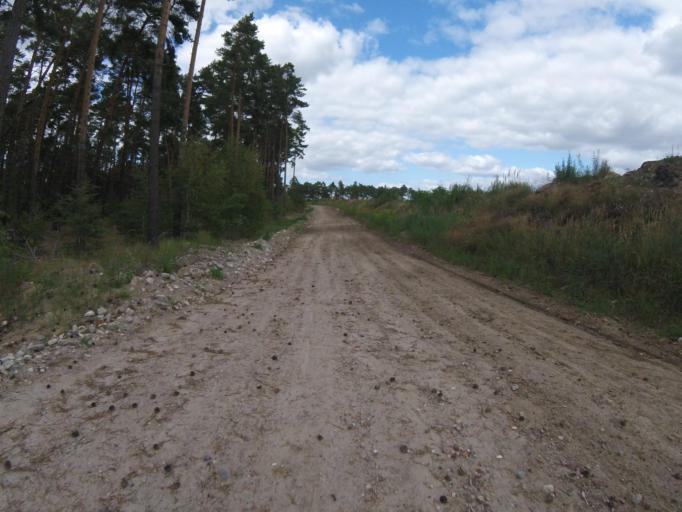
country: DE
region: Brandenburg
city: Wildau
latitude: 52.3282
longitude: 13.6768
